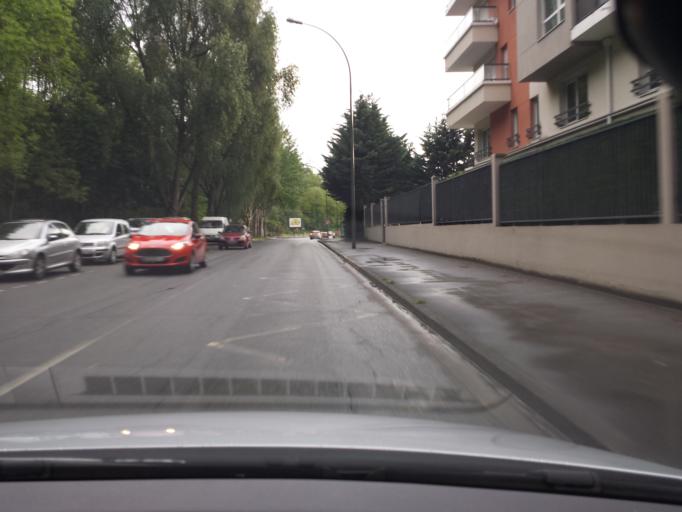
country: FR
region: Ile-de-France
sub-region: Departement de l'Essonne
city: Verrieres-le-Buisson
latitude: 48.7360
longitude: 2.2714
